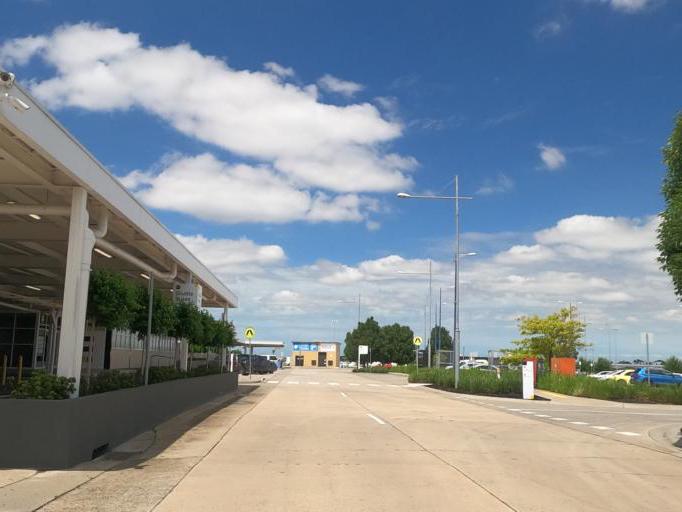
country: AU
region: Victoria
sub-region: Moonee Valley
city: Niddrie
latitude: -37.7268
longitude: 144.8969
